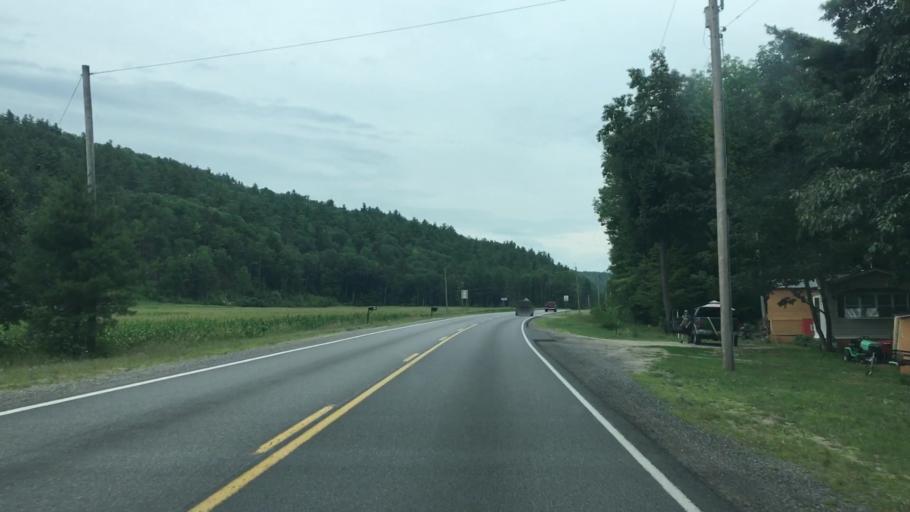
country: US
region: New York
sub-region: Clinton County
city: Peru
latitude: 44.5140
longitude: -73.5815
